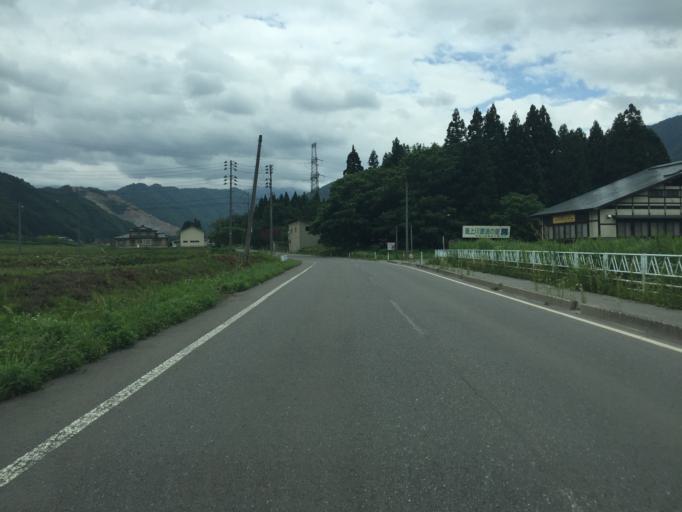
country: JP
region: Yamagata
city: Yonezawa
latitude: 37.8405
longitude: 140.0921
